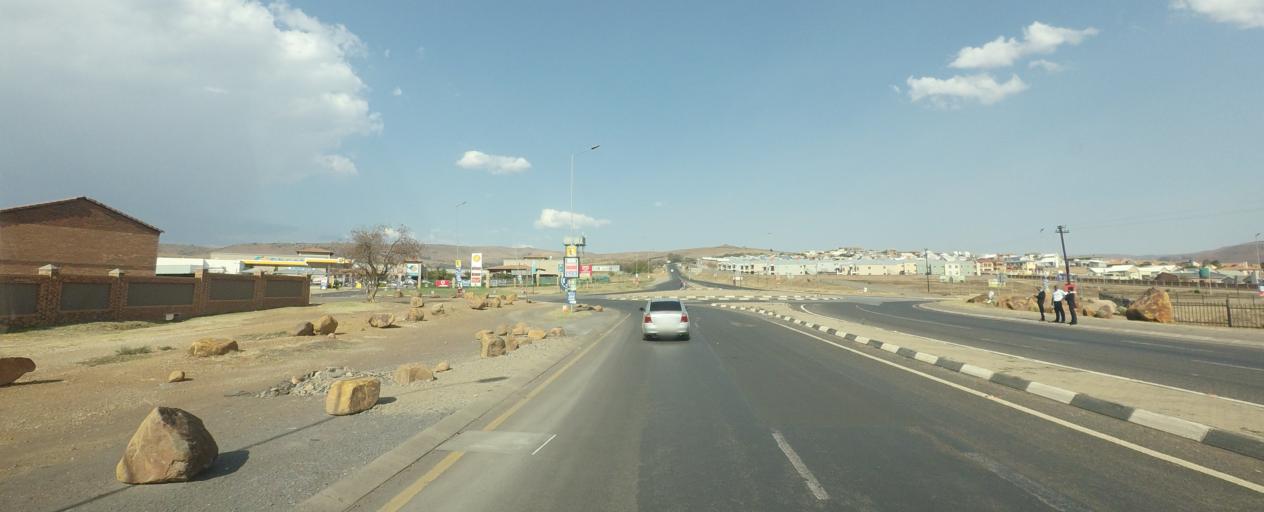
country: ZA
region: Mpumalanga
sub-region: Ehlanzeni District
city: Lydenburg
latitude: -25.1038
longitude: 30.4814
